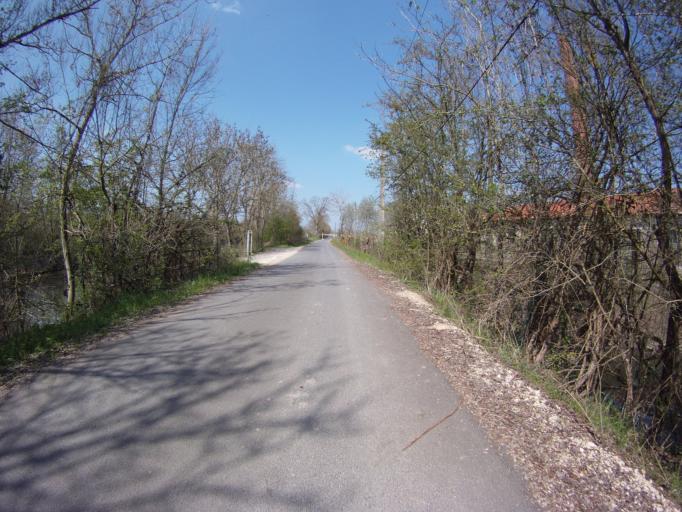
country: FR
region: Lorraine
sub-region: Departement de Meurthe-et-Moselle
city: Blenod-les-Pont-a-Mousson
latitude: 48.8731
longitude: 6.0687
